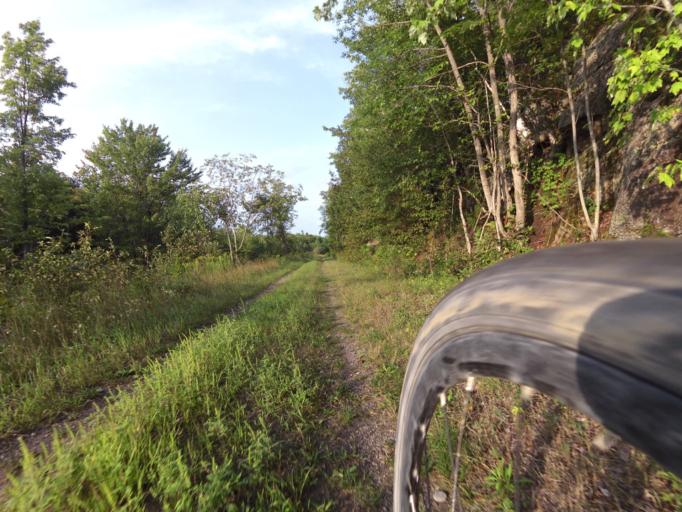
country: CA
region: Ontario
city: Gananoque
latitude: 44.5460
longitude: -76.3941
